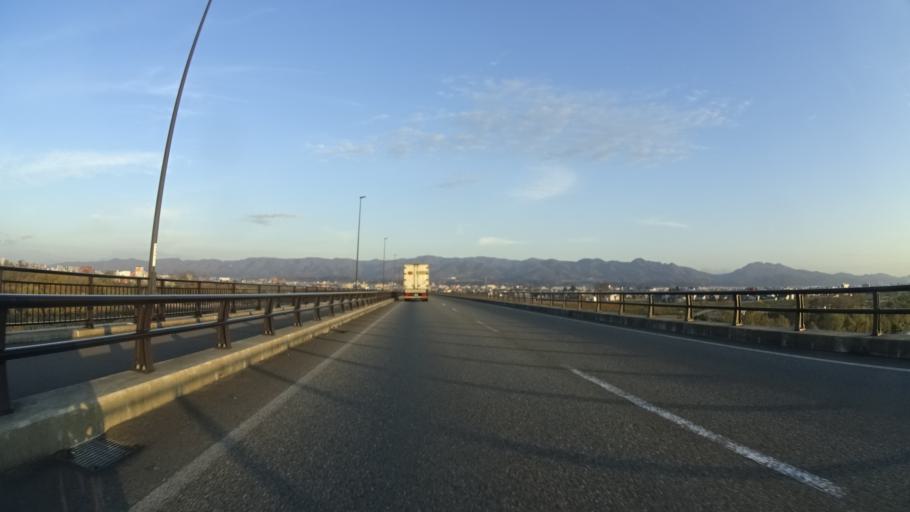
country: JP
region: Niigata
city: Nagaoka
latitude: 37.4305
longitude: 138.8232
